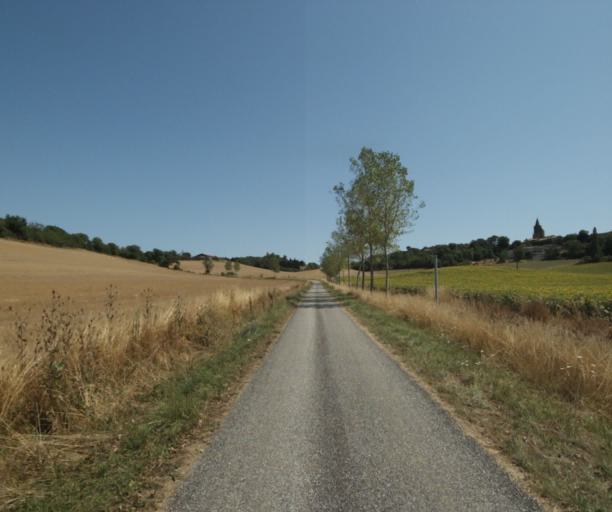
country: FR
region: Midi-Pyrenees
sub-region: Departement de la Haute-Garonne
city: Saint-Felix-Lauragais
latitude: 43.4538
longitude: 1.8838
